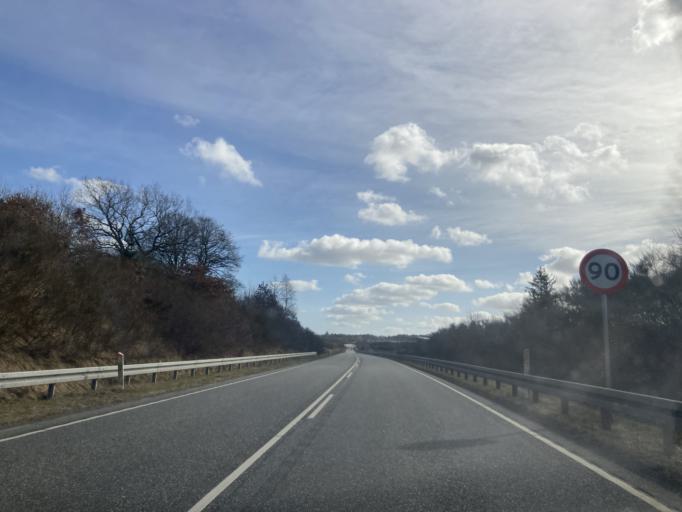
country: DK
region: Central Jutland
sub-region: Hedensted Kommune
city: Torring
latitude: 55.9757
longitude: 9.3958
